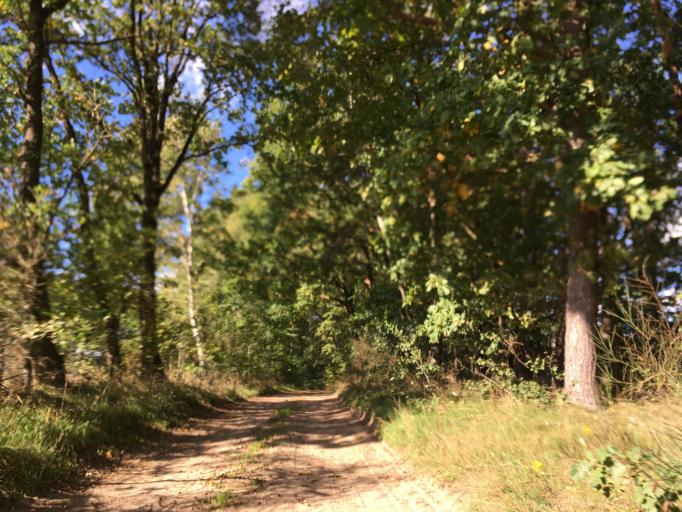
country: DE
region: Lower Saxony
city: Barendorf
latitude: 53.2186
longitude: 10.5010
